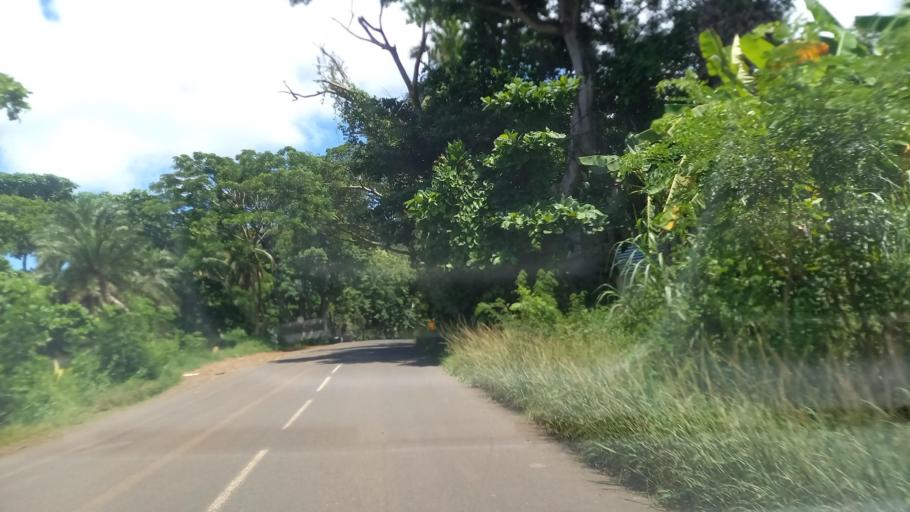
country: YT
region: Sada
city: Sada
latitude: -12.8666
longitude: 45.1141
